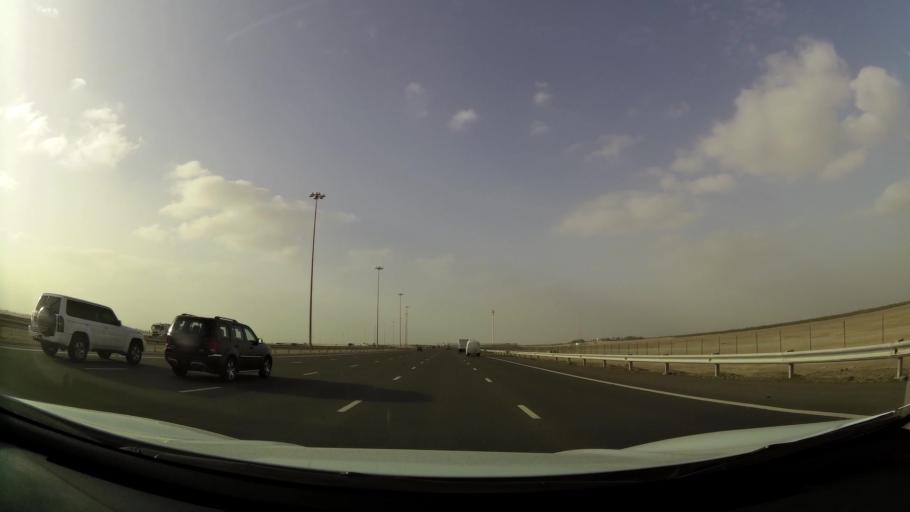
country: AE
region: Abu Dhabi
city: Abu Dhabi
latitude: 24.5376
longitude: 54.4853
